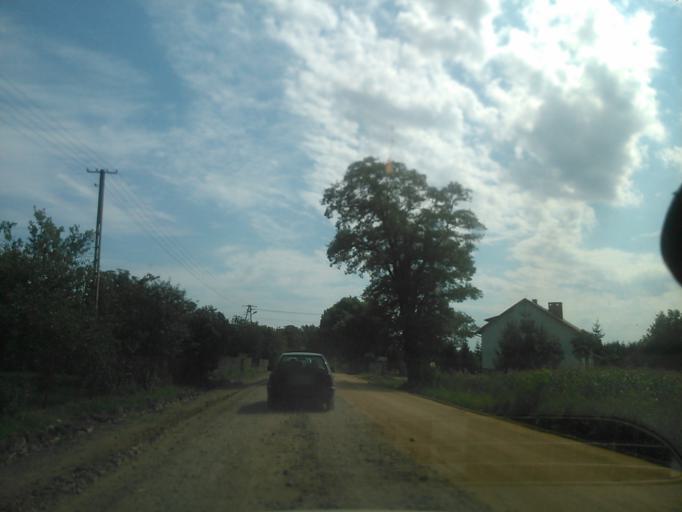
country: PL
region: Warmian-Masurian Voivodeship
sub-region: Powiat dzialdowski
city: Ilowo -Osada
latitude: 53.1992
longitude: 20.2486
